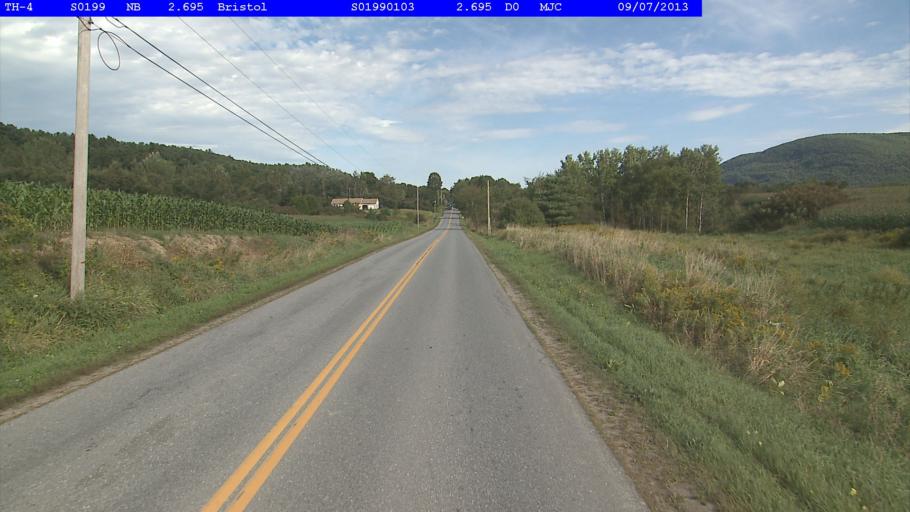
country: US
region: Vermont
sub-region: Addison County
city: Bristol
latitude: 44.1670
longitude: -73.1008
